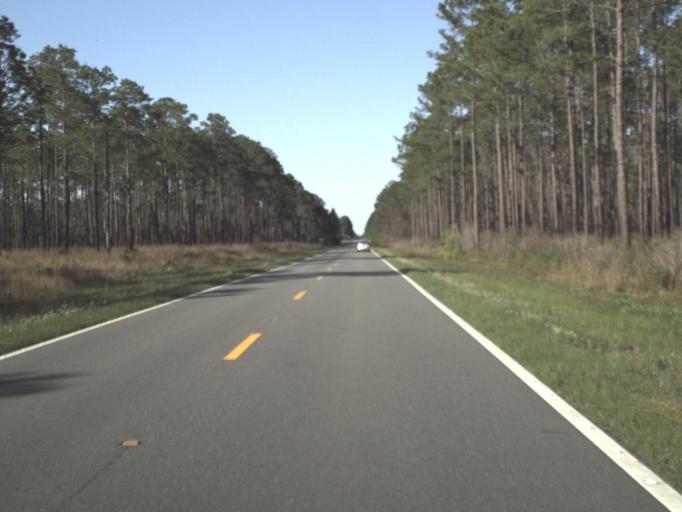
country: US
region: Florida
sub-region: Gulf County
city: Wewahitchka
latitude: 30.1482
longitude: -84.9721
